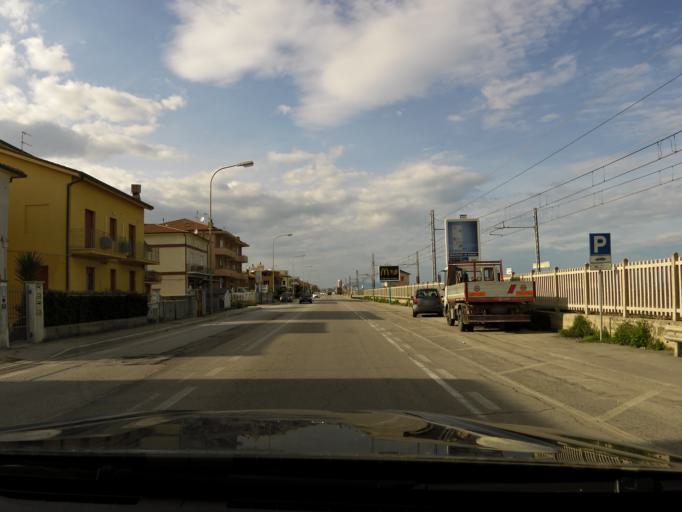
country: IT
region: The Marches
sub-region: Provincia di Macerata
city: Porto Potenza Picena
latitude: 43.3344
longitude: 13.7107
